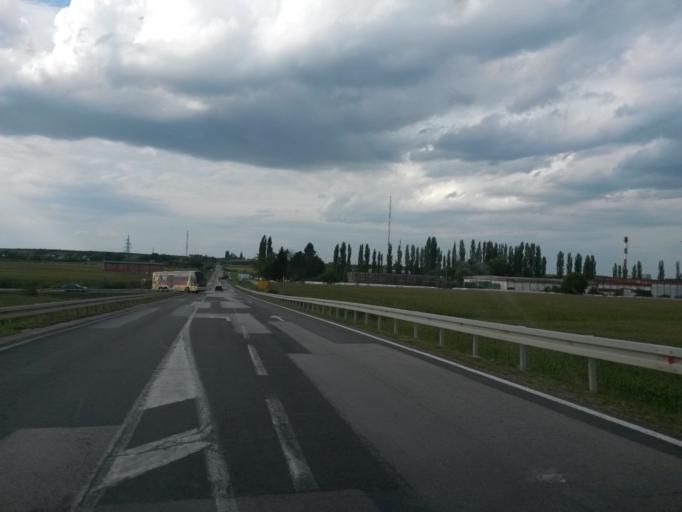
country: HR
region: Vukovarsko-Srijemska
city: Jarmina
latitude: 45.2918
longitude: 18.7407
